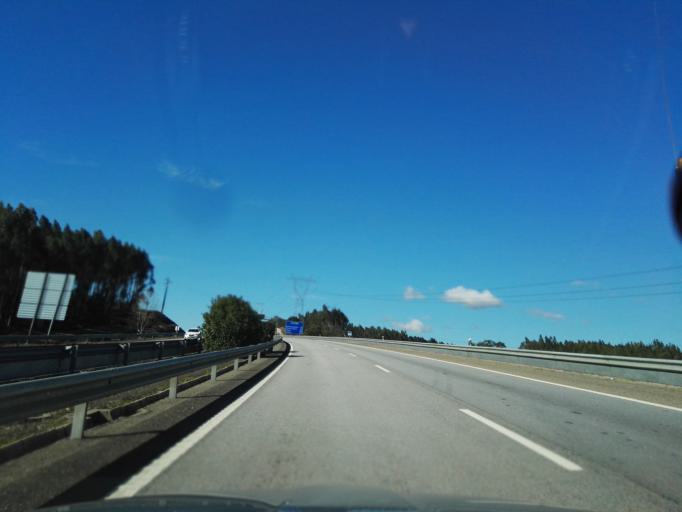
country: PT
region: Santarem
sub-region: Abrantes
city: Alferrarede
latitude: 39.4947
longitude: -8.1835
